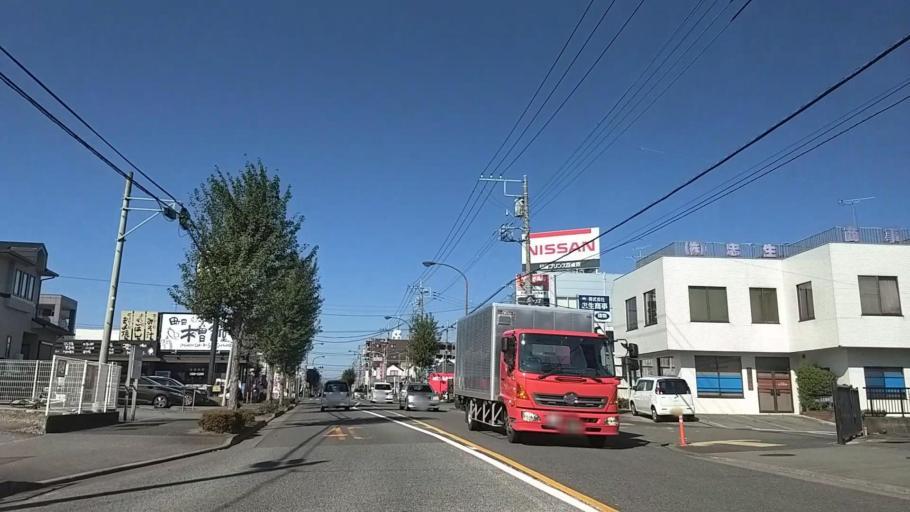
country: JP
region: Tokyo
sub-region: Machida-shi
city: Machida
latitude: 35.5746
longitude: 139.4187
